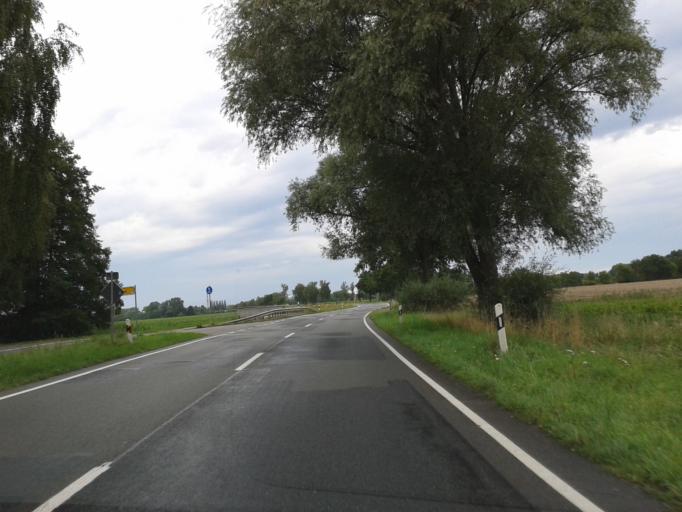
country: DE
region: Lower Saxony
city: Woltersdorf
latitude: 52.9599
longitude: 11.1858
